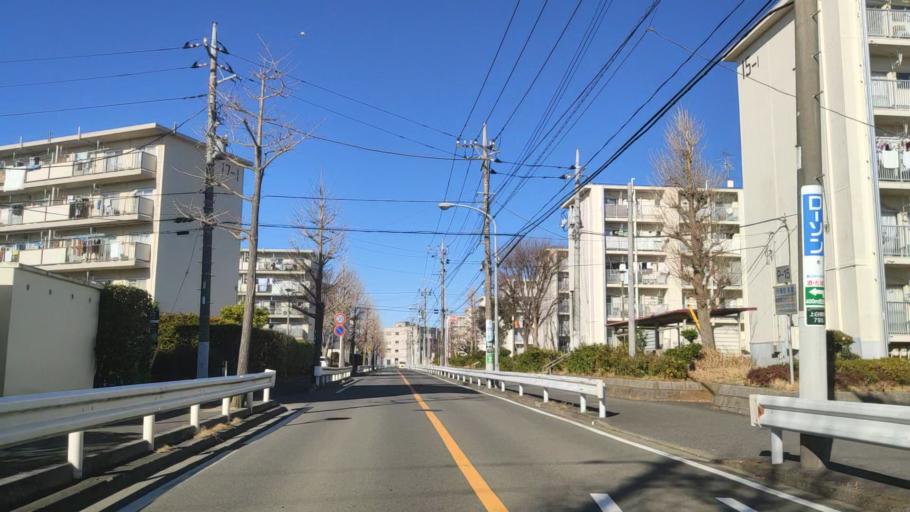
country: JP
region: Kanagawa
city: Minami-rinkan
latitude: 35.5005
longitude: 139.5301
